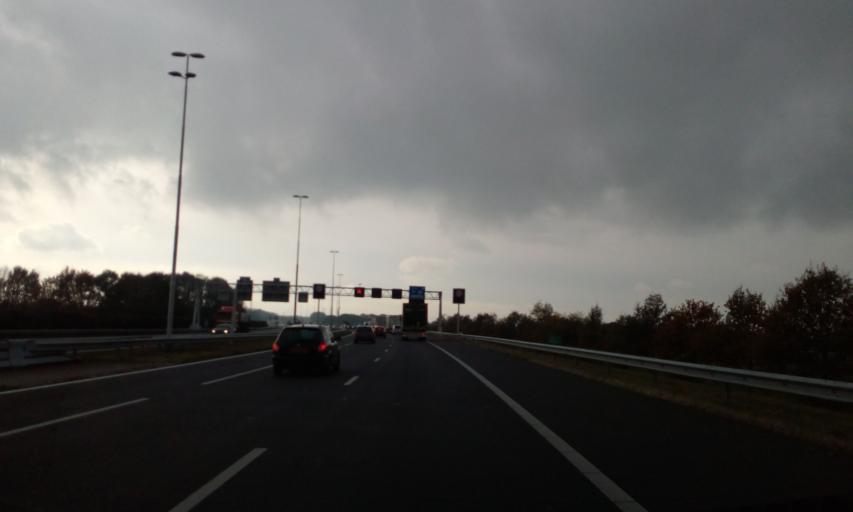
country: NL
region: Gelderland
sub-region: Gemeente Voorst
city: Twello
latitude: 52.2155
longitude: 6.1127
